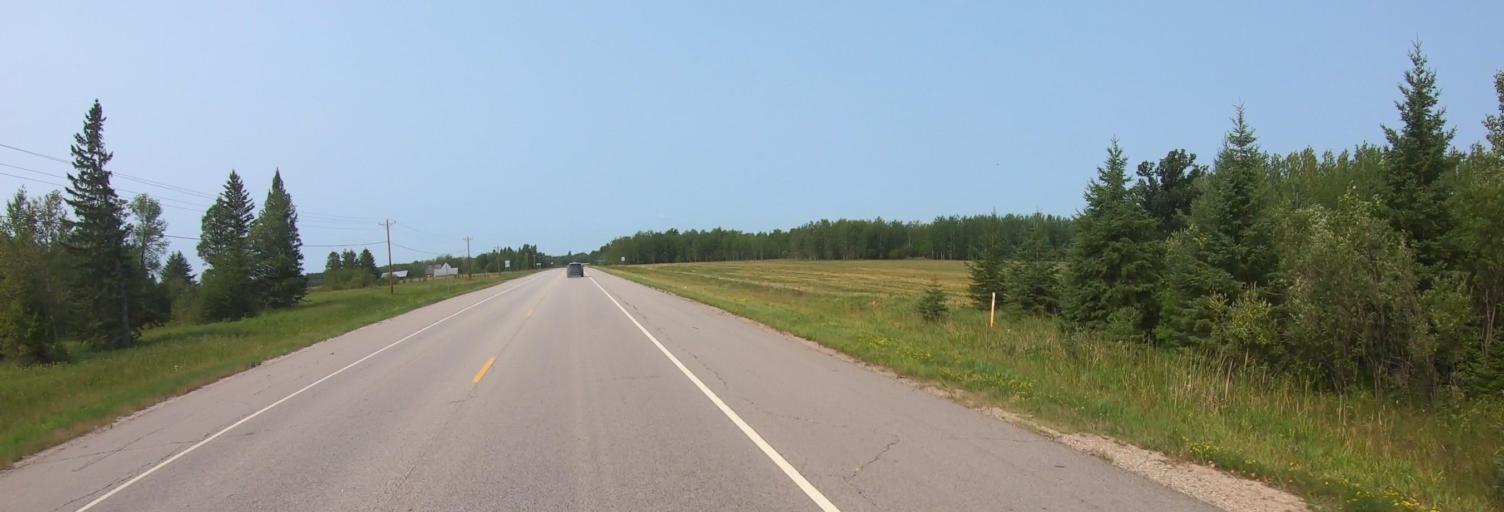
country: CA
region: Ontario
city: Fort Frances
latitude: 48.4891
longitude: -93.3339
